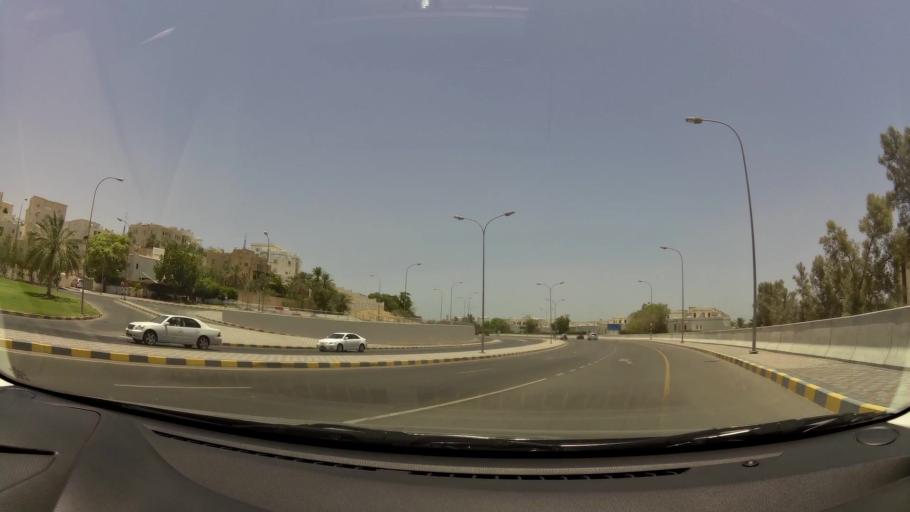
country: OM
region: Muhafazat Masqat
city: Bawshar
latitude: 23.5955
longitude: 58.4574
